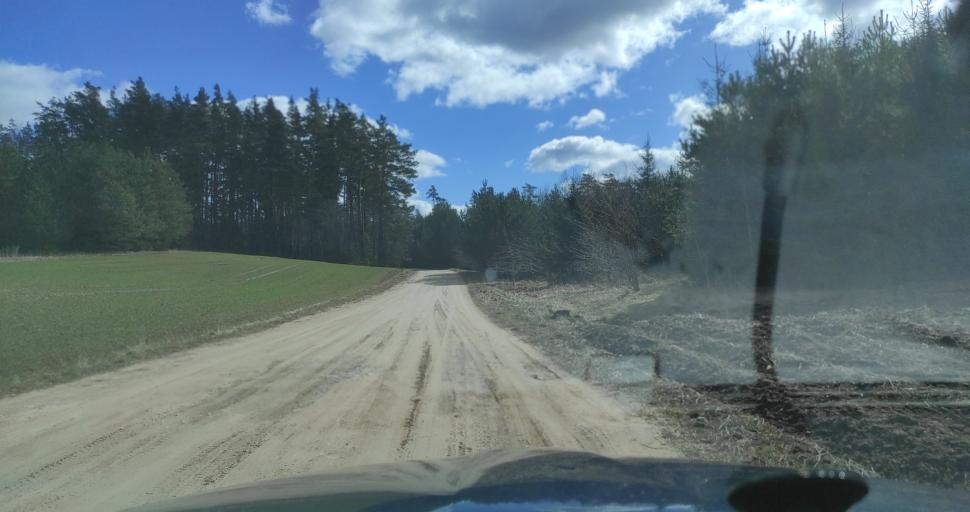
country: LV
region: Kuldigas Rajons
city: Kuldiga
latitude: 56.9555
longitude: 21.9239
